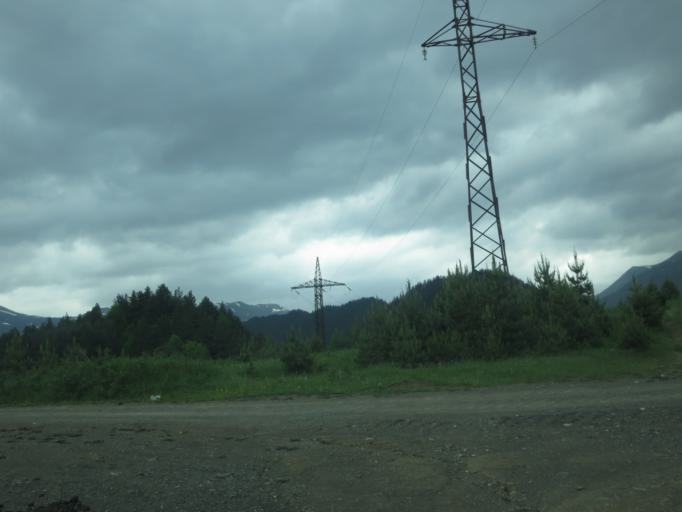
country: RU
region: Chechnya
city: Itum-Kali
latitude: 42.3683
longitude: 45.6272
